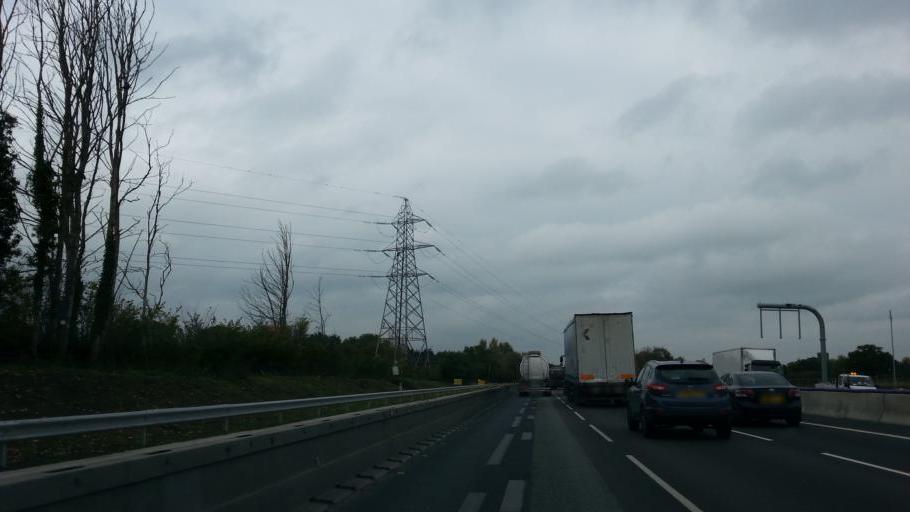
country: GB
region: England
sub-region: Cheshire East
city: Knutsford
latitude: 53.2591
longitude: -2.4026
